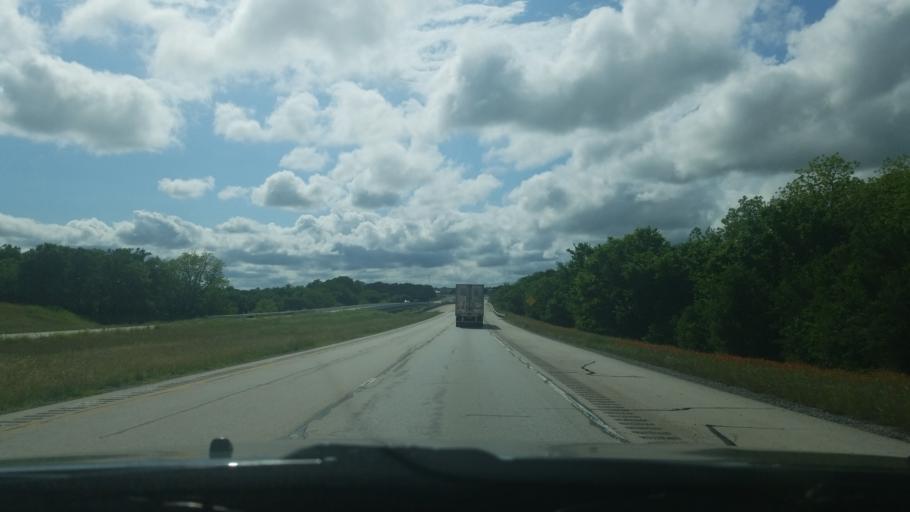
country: US
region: Texas
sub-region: Denton County
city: Ponder
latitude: 33.2487
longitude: -97.4010
